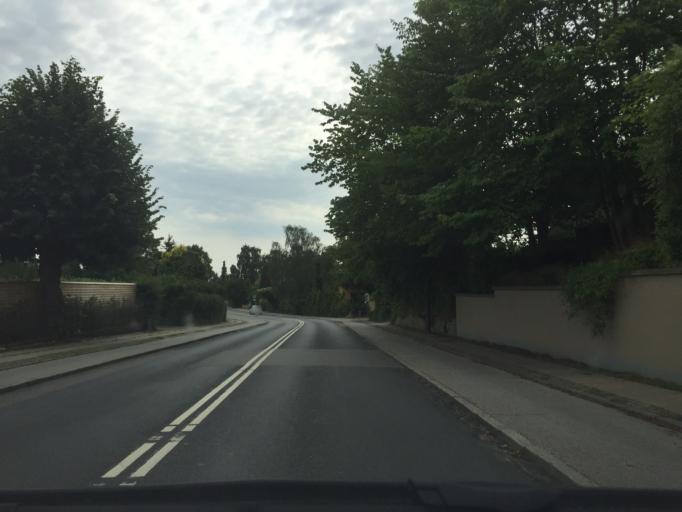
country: DK
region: Capital Region
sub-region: Gentofte Kommune
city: Charlottenlund
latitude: 55.7673
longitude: 12.5594
